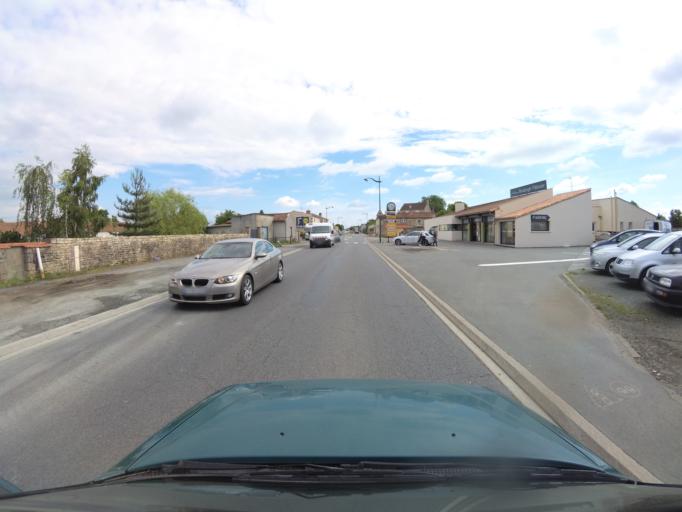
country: FR
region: Pays de la Loire
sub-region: Departement de la Vendee
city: Sainte-Gemme-la-Plaine
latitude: 46.4815
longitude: -1.1118
